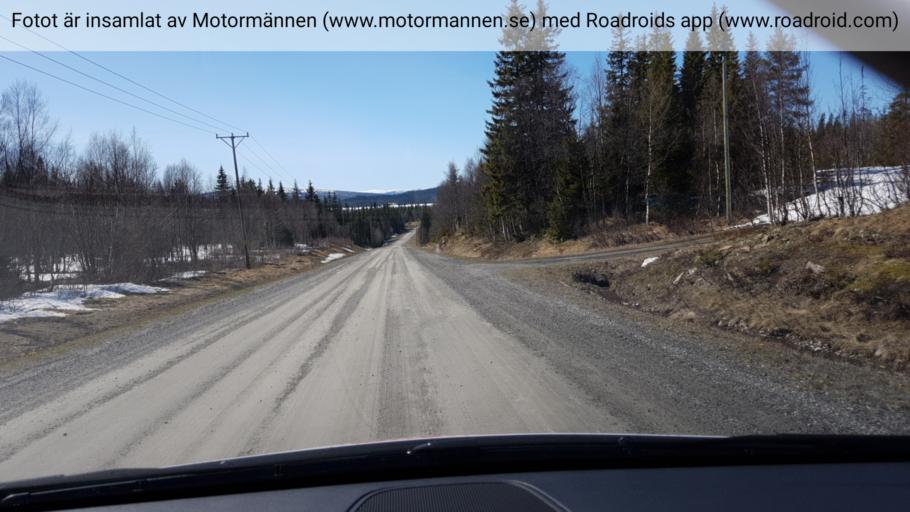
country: SE
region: Jaemtland
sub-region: Are Kommun
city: Are
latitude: 63.7031
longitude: 12.6743
